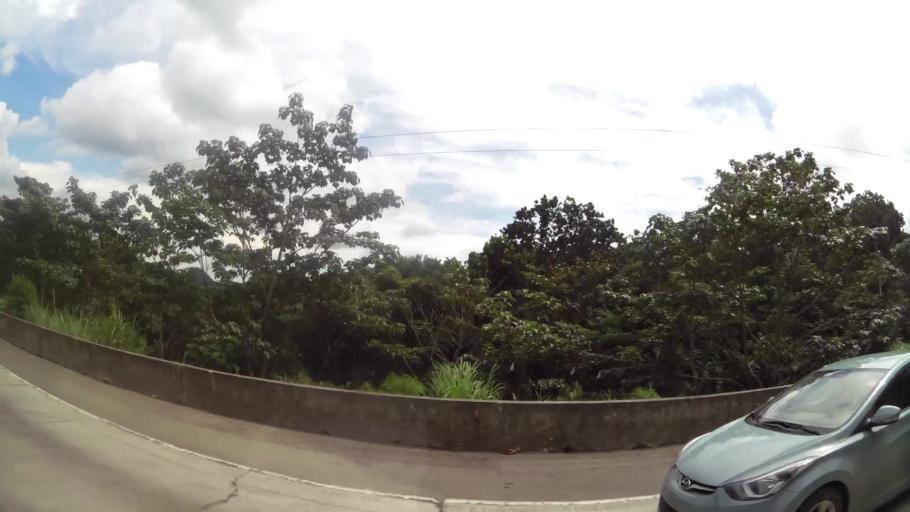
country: PA
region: Panama
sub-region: Distrito de Panama
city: Paraiso
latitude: 9.0096
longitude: -79.6474
